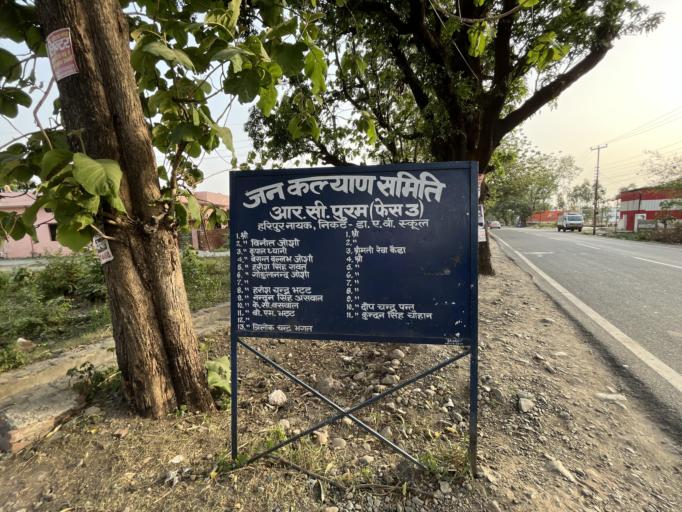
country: IN
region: Uttarakhand
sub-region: Naini Tal
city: Haldwani
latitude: 29.2179
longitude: 79.4891
